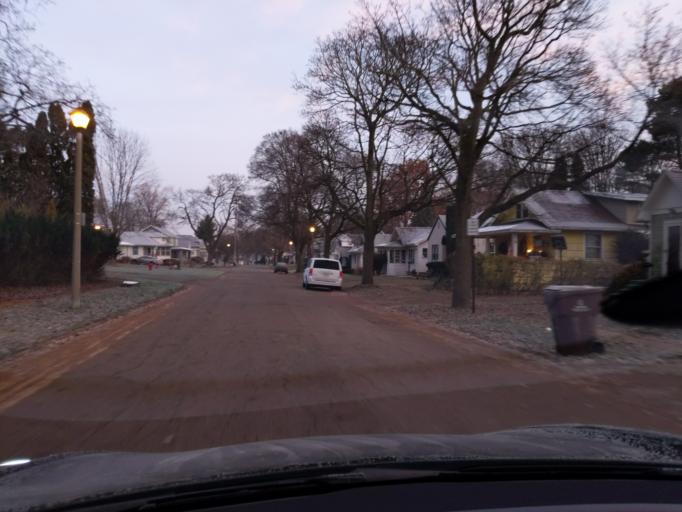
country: US
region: Michigan
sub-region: Ingham County
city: Lansing
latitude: 42.7058
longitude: -84.5534
